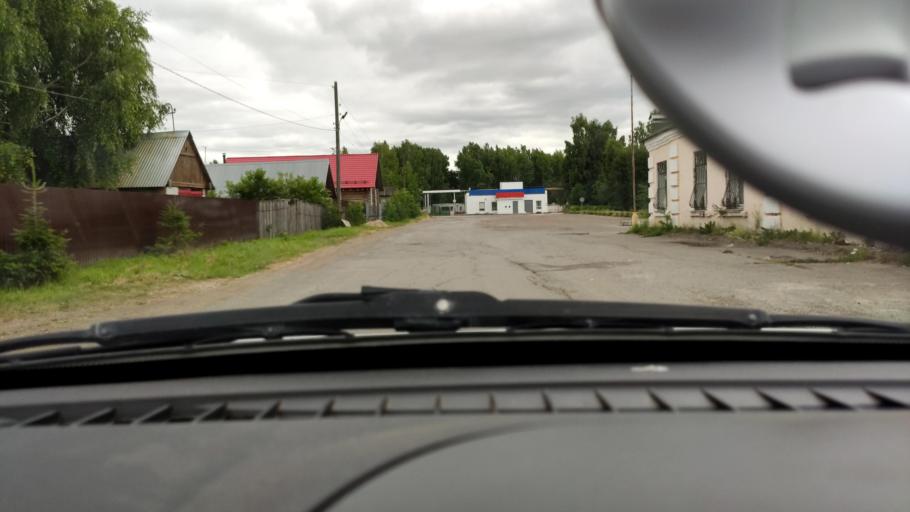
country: RU
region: Perm
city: Ferma
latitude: 57.8933
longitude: 56.2970
